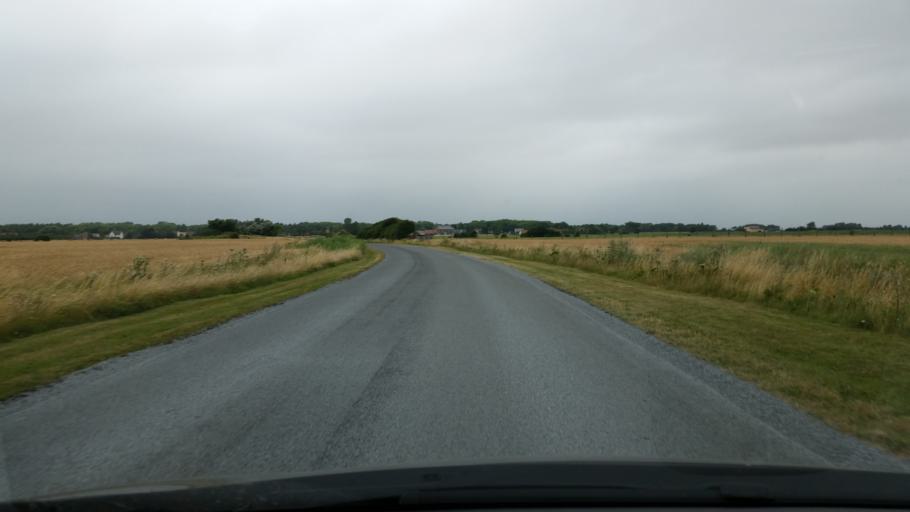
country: FR
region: Nord-Pas-de-Calais
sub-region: Departement du Pas-de-Calais
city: Marck
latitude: 50.9595
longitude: 1.9400
